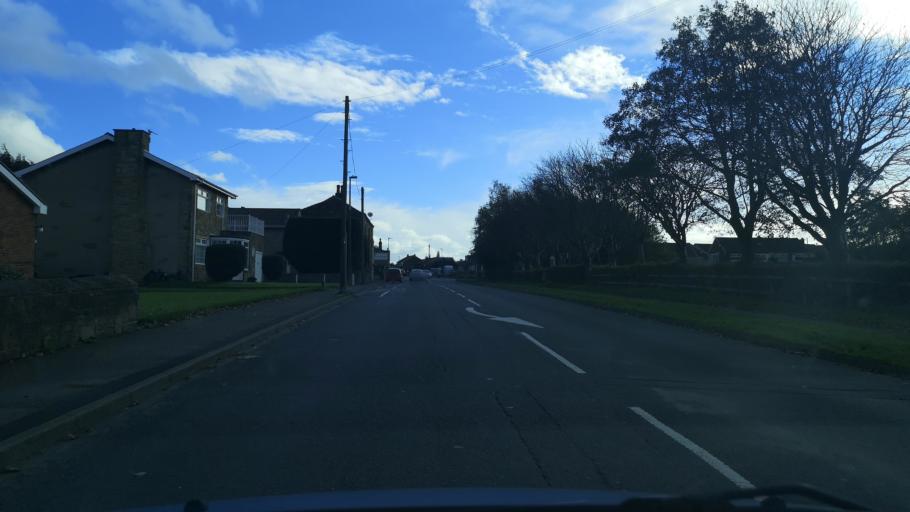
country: GB
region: England
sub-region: Kirklees
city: Heckmondwike
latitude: 53.7205
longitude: -1.6643
